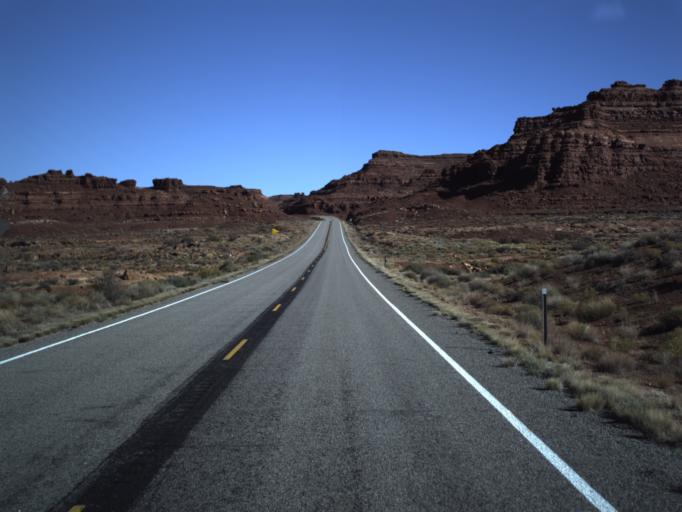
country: US
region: Utah
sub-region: San Juan County
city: Blanding
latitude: 37.8473
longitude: -110.3546
